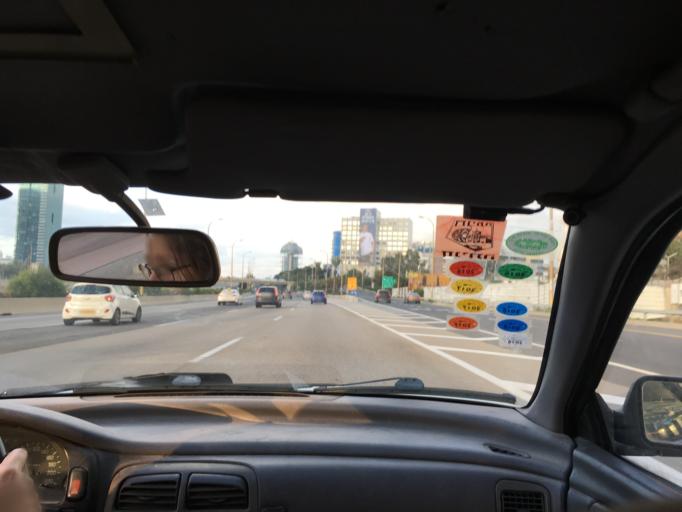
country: IL
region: Tel Aviv
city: Ramat Gan
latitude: 32.0862
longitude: 34.7998
